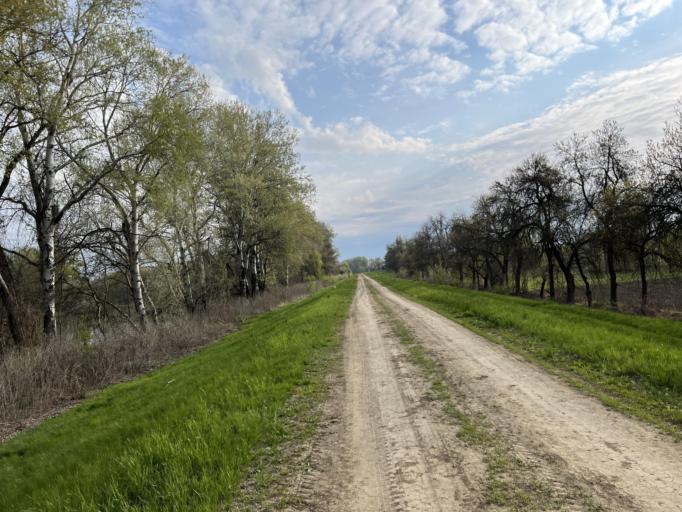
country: HU
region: Jasz-Nagykun-Szolnok
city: Szajol
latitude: 47.1890
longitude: 20.2919
